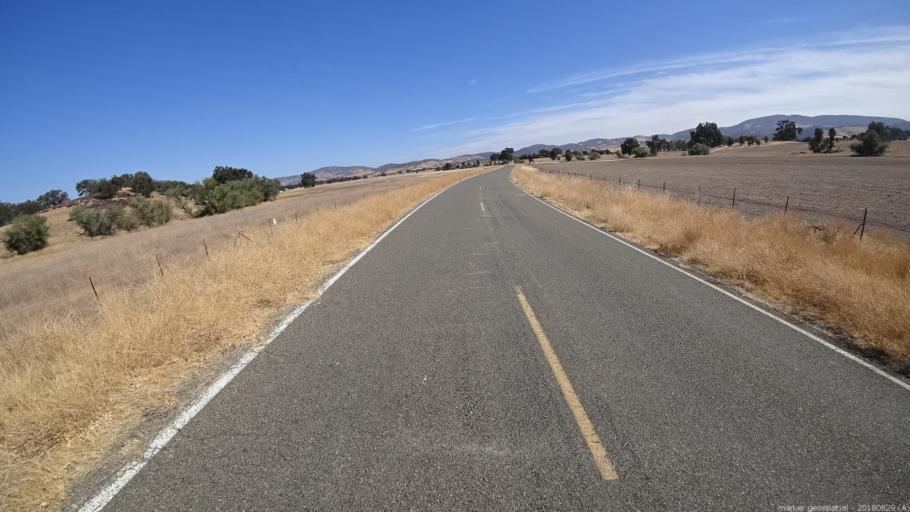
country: US
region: California
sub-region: San Luis Obispo County
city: Lake Nacimiento
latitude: 35.9209
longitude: -121.0839
